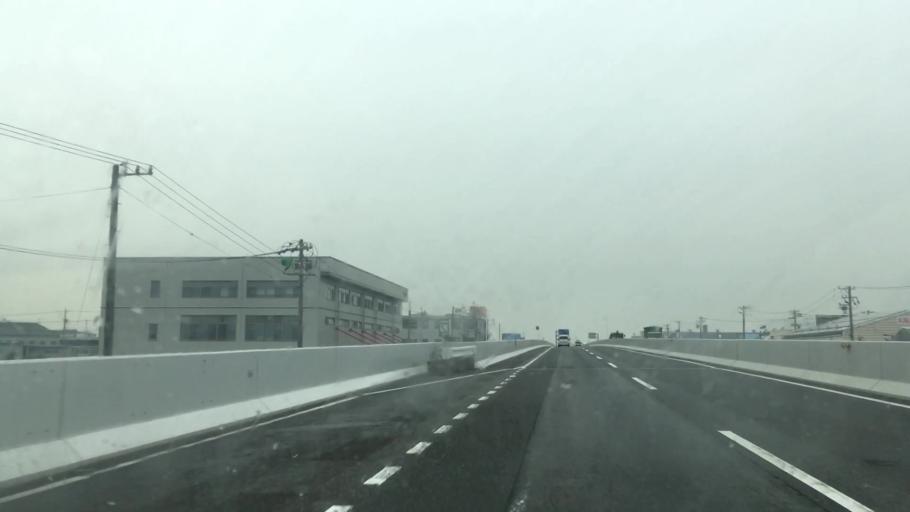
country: JP
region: Aichi
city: Anjo
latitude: 34.9182
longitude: 137.0560
